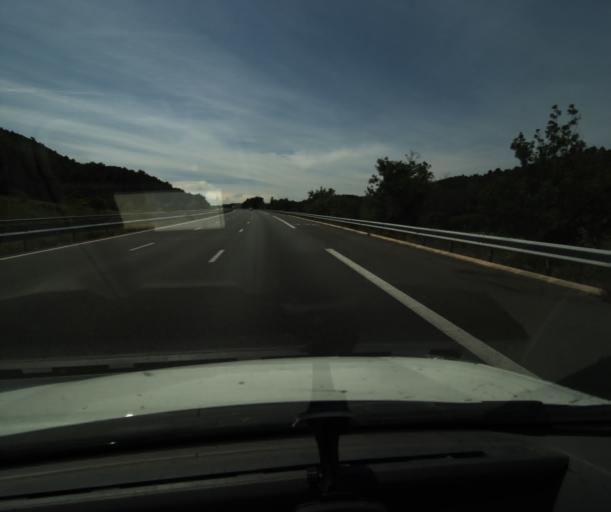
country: FR
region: Languedoc-Roussillon
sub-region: Departement de l'Aude
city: Puicheric
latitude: 43.1746
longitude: 2.6346
